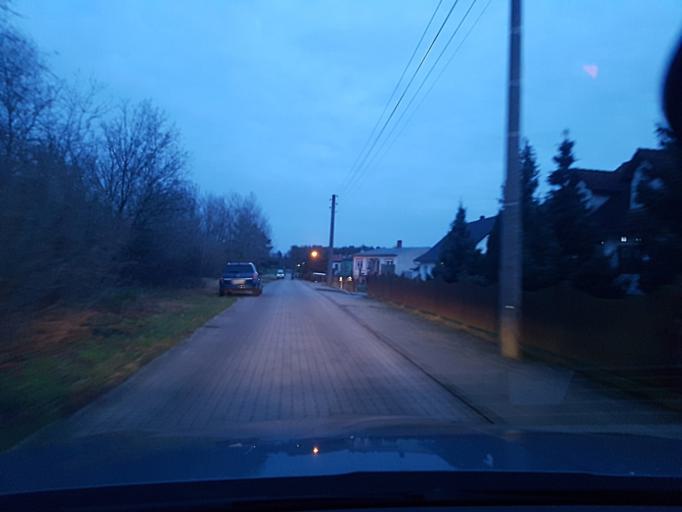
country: DE
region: Brandenburg
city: Ruckersdorf
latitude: 51.5918
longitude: 13.5474
